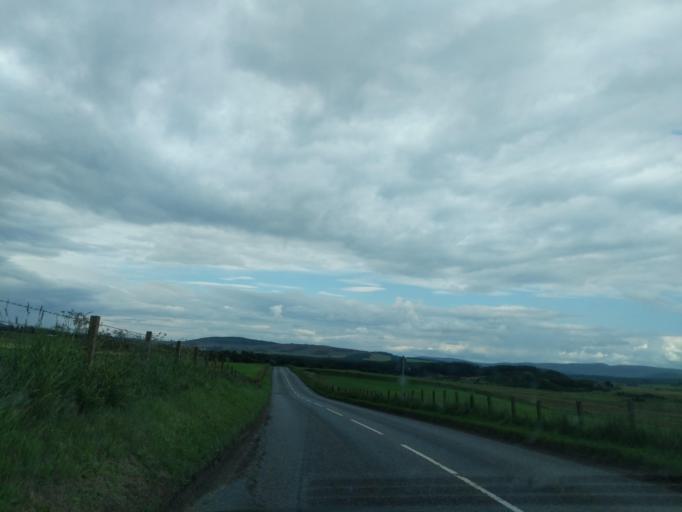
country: GB
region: Scotland
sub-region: Highland
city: Aviemore
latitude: 57.2987
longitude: -3.7594
